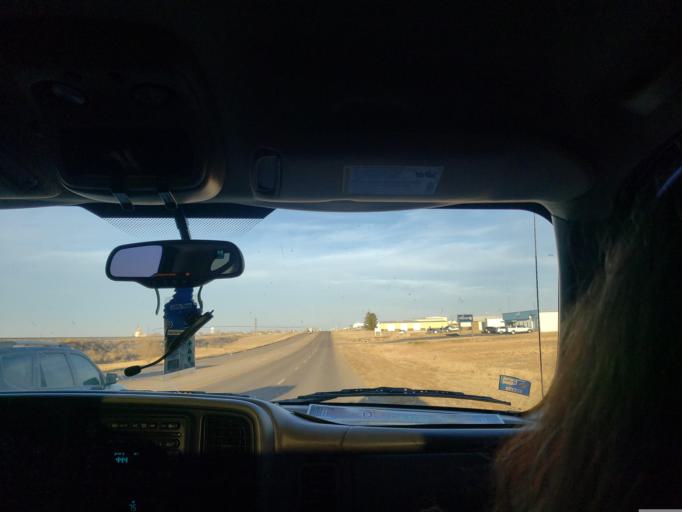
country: US
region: Oklahoma
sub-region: Texas County
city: Guymon
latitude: 36.6930
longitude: -101.4633
